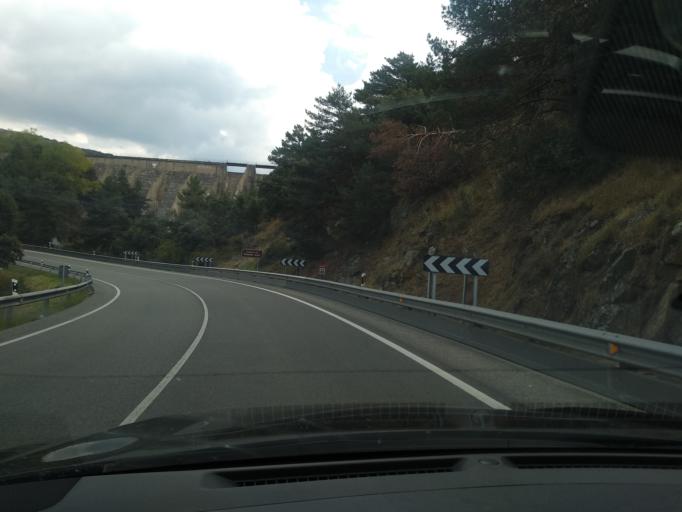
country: ES
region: Castille and Leon
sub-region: Provincia de Segovia
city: Palazuelos de Eresma
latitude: 40.8625
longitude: -4.0991
